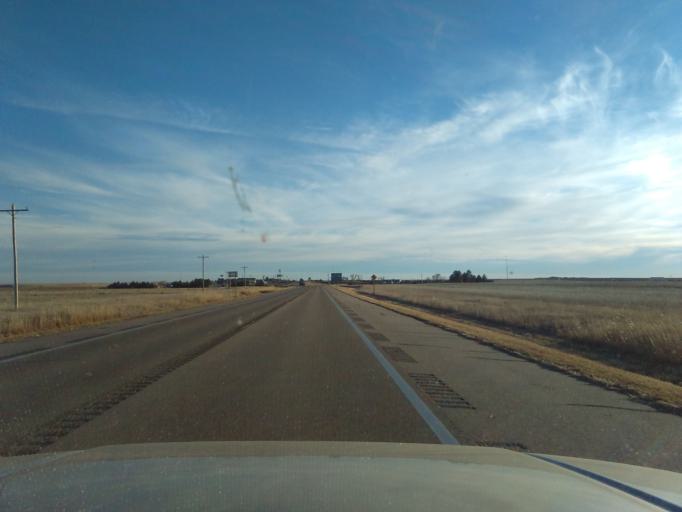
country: US
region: Kansas
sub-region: Logan County
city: Oakley
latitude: 39.1973
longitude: -100.8701
